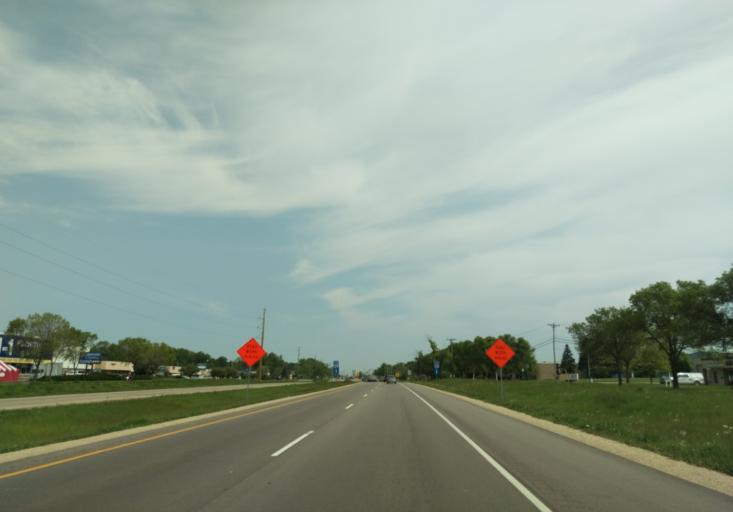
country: US
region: Wisconsin
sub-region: Dane County
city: Monona
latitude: 43.0681
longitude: -89.3092
